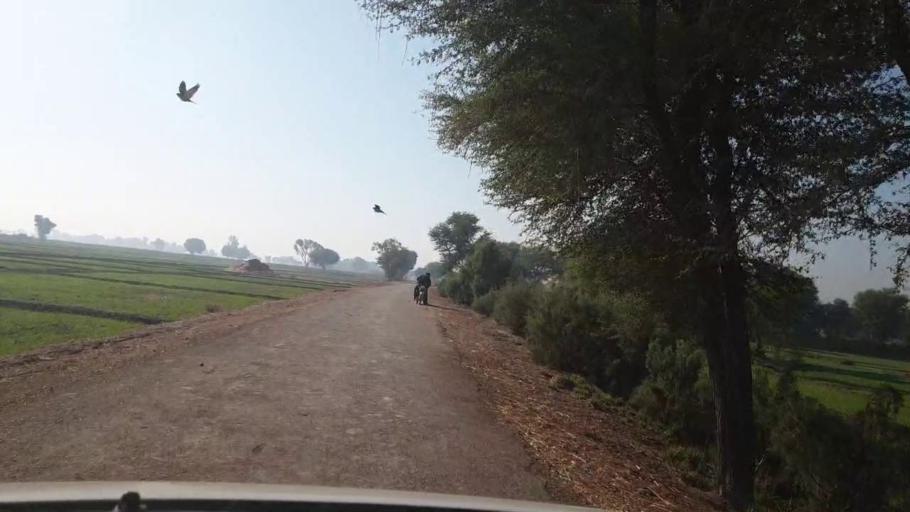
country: PK
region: Sindh
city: Dadu
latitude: 26.6546
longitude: 67.8226
